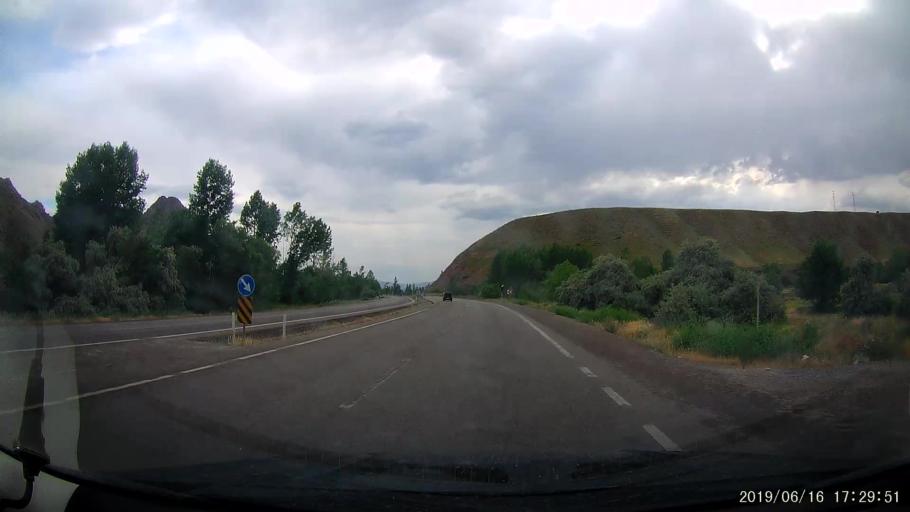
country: TR
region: Erzincan
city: Tercan
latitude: 39.7803
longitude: 40.3581
